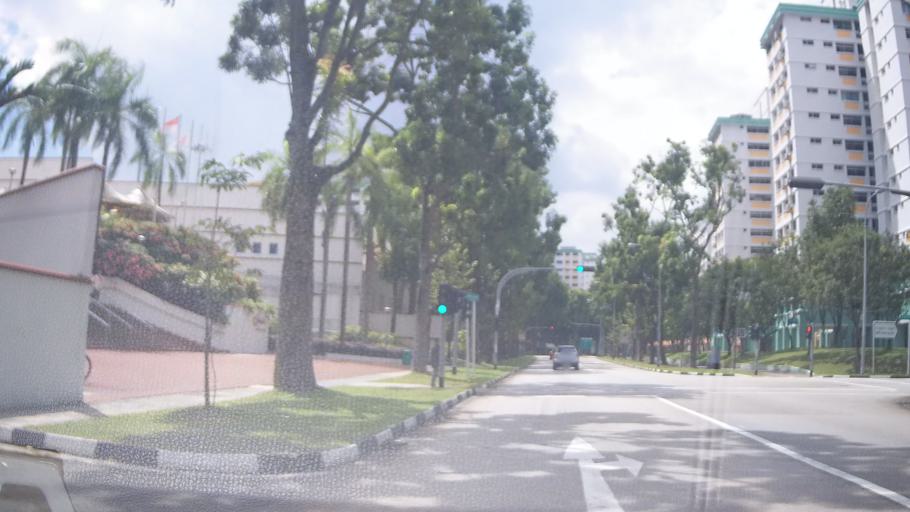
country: MY
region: Johor
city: Johor Bahru
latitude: 1.3921
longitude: 103.7487
